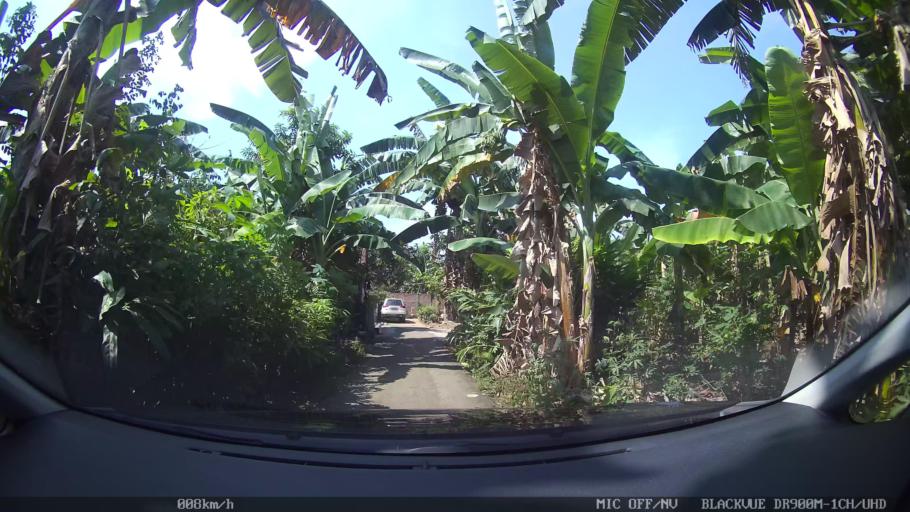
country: ID
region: Lampung
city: Kedaton
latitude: -5.3656
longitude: 105.2549
